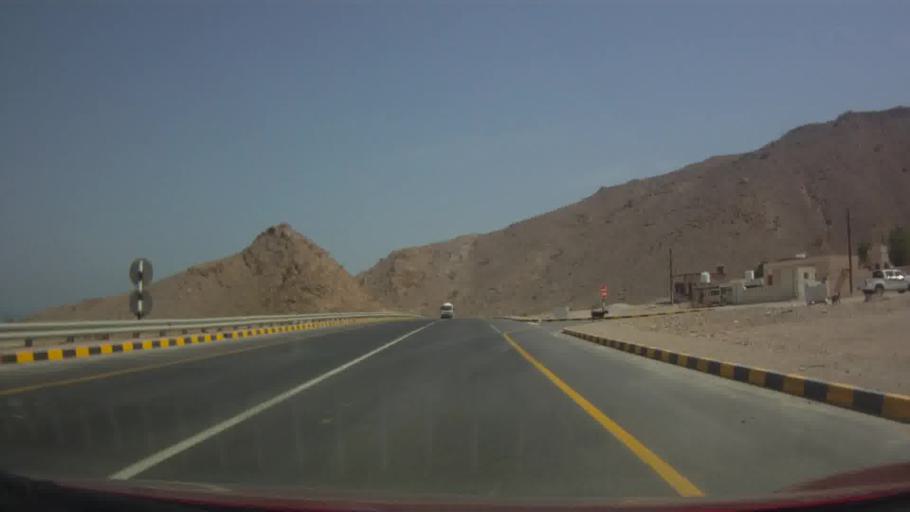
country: OM
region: Muhafazat Masqat
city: Muscat
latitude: 23.3894
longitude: 58.8010
